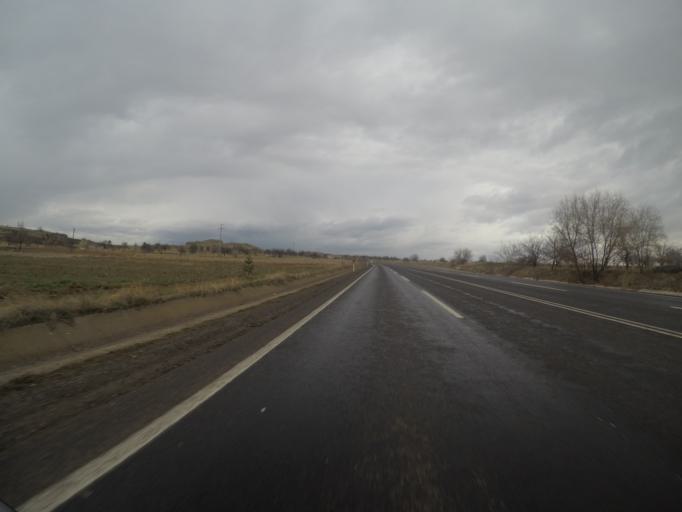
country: TR
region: Nevsehir
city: Urgub
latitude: 38.6351
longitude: 34.8766
